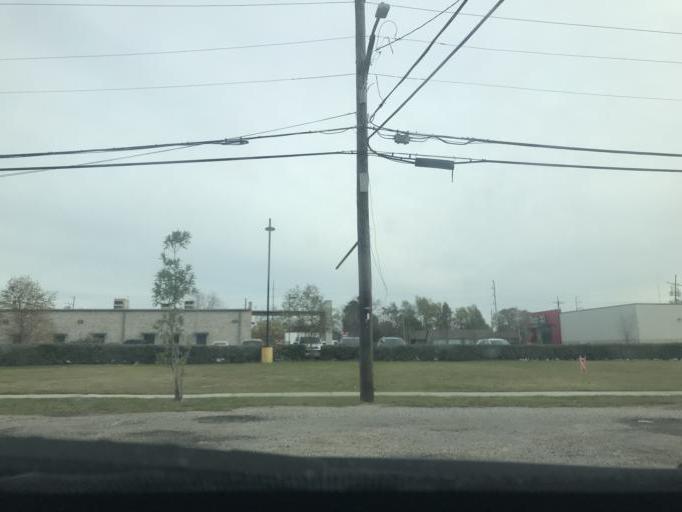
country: US
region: Louisiana
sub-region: Orleans Parish
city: New Orleans
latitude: 29.9586
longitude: -90.1123
